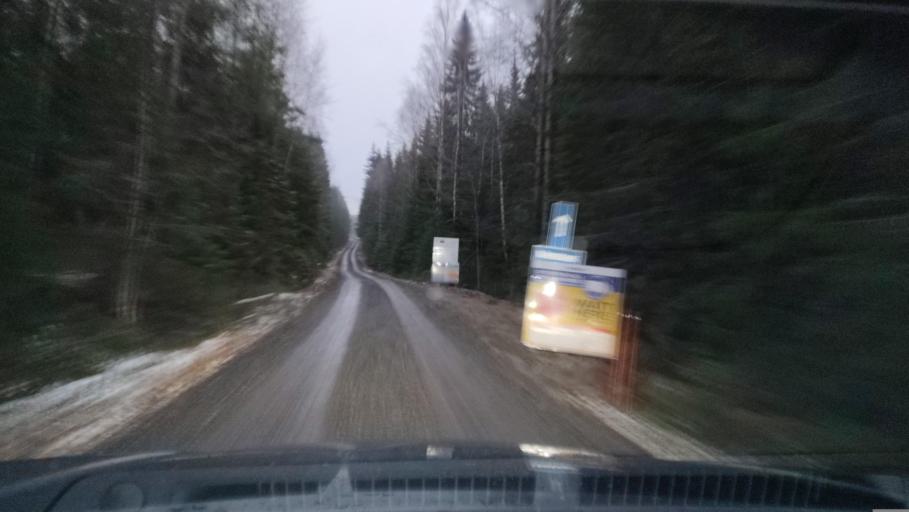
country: FI
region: Southern Ostrobothnia
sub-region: Suupohja
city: Karijoki
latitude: 62.1403
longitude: 21.6274
